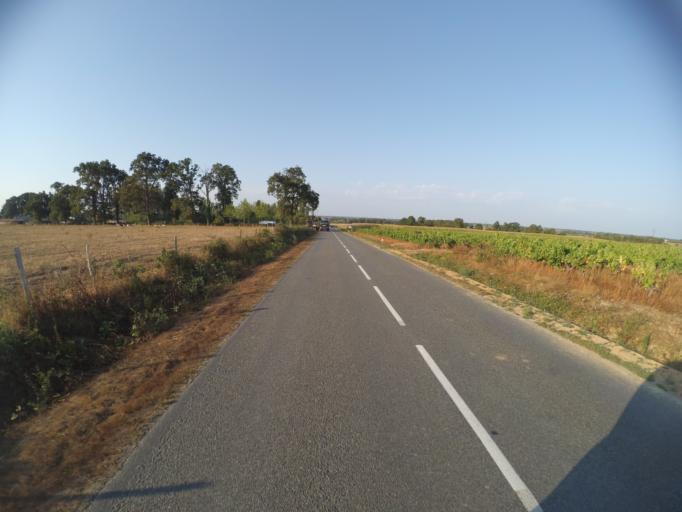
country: FR
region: Pays de la Loire
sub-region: Departement de la Loire-Atlantique
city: La Planche
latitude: 47.0315
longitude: -1.4196
